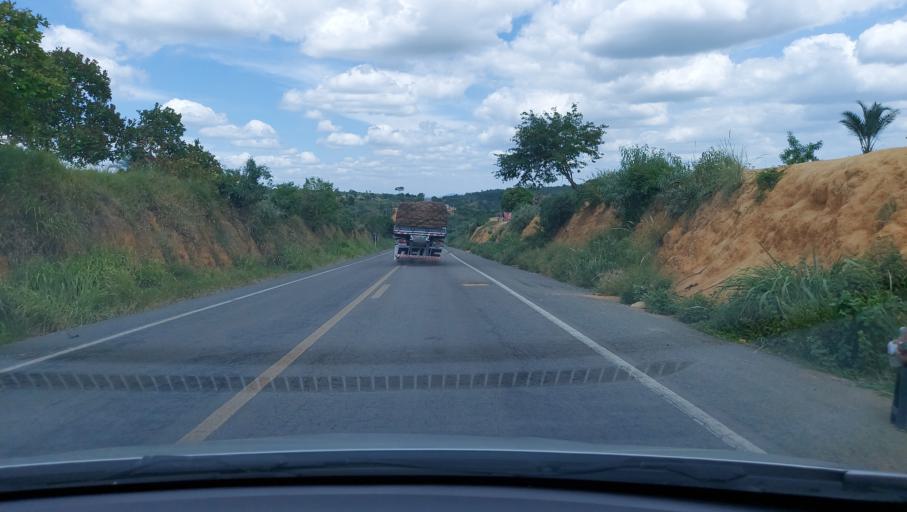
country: BR
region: Bahia
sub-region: Ruy Barbosa
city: Terra Nova
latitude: -12.4421
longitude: -40.7815
